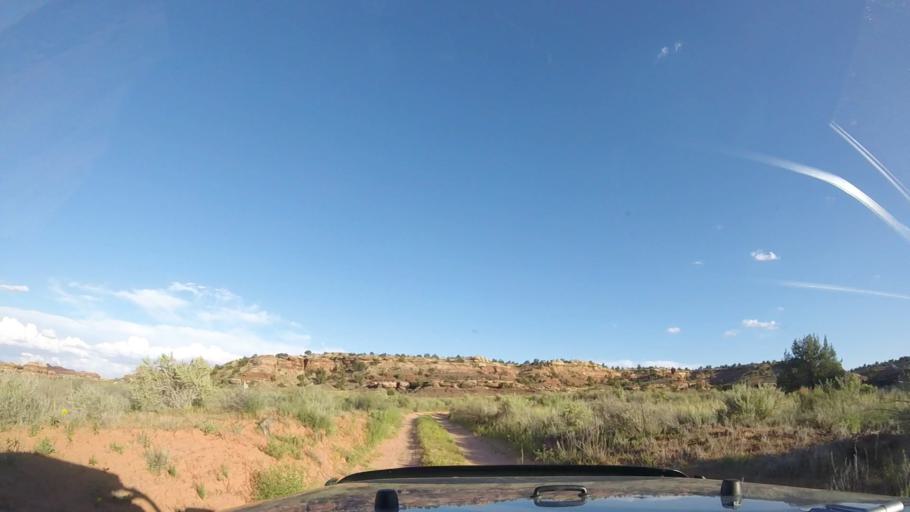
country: US
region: Utah
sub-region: Grand County
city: Moab
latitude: 38.1932
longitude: -109.7840
